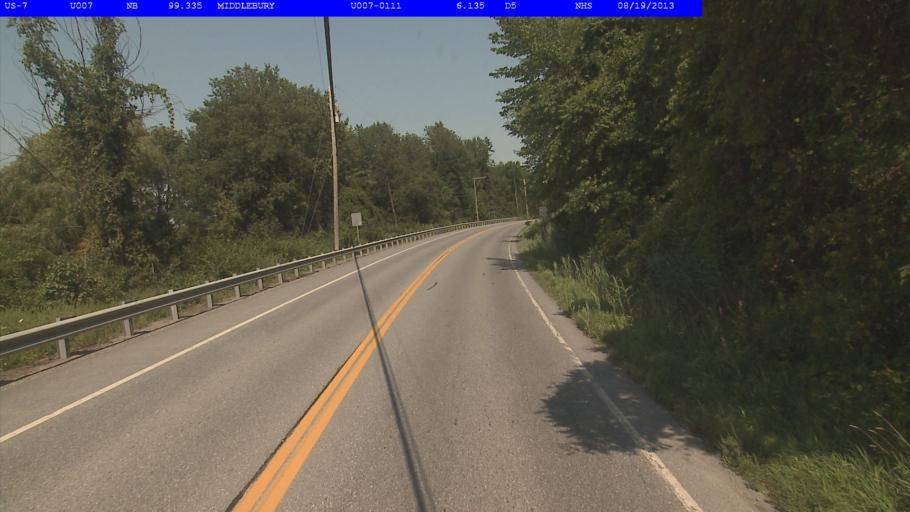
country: US
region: Vermont
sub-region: Addison County
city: Middlebury (village)
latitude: 44.0289
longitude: -73.1676
